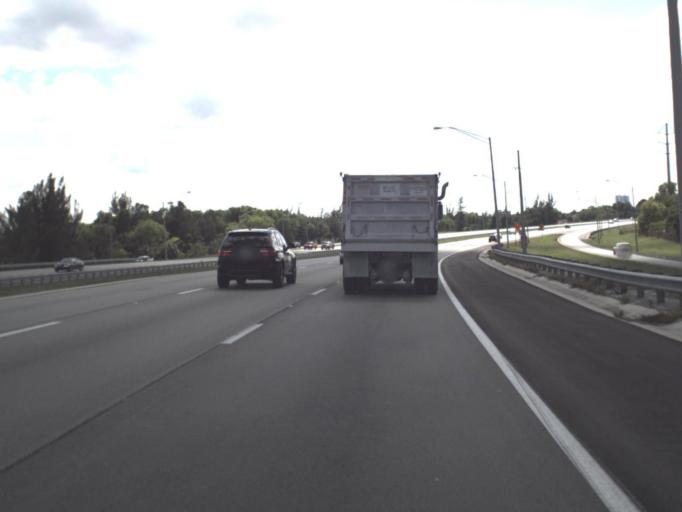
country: US
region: Florida
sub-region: Broward County
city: Tamarac
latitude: 26.1917
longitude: -80.2954
